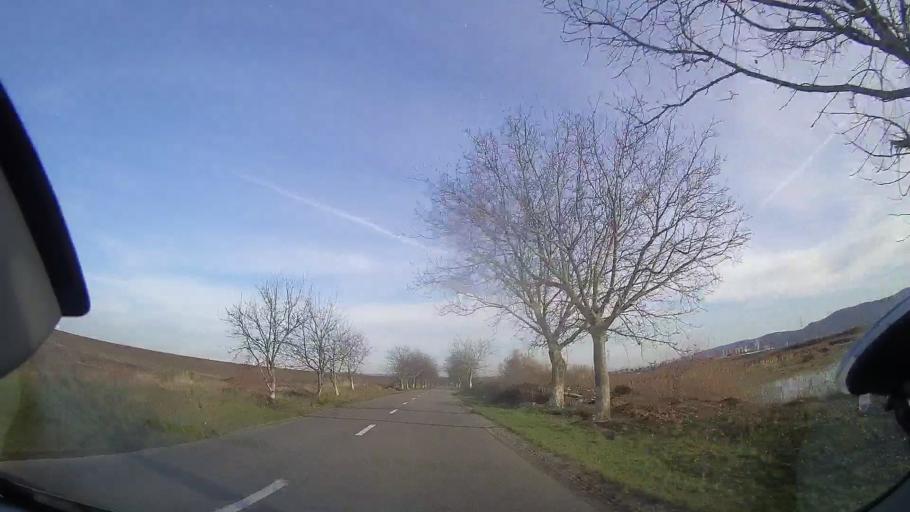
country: RO
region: Bihor
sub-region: Comuna Tetchea
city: Hotar
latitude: 47.0518
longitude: 22.3017
